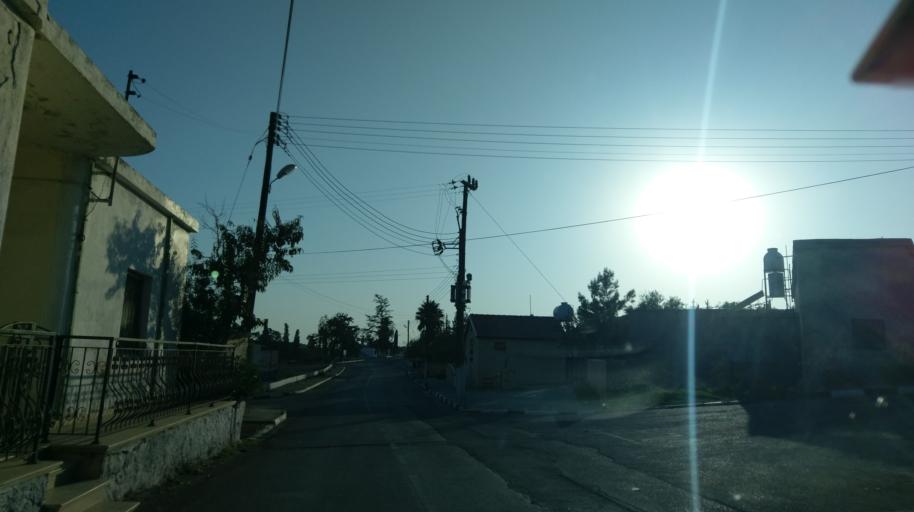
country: CY
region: Ammochostos
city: Leonarisso
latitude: 35.4097
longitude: 33.9954
